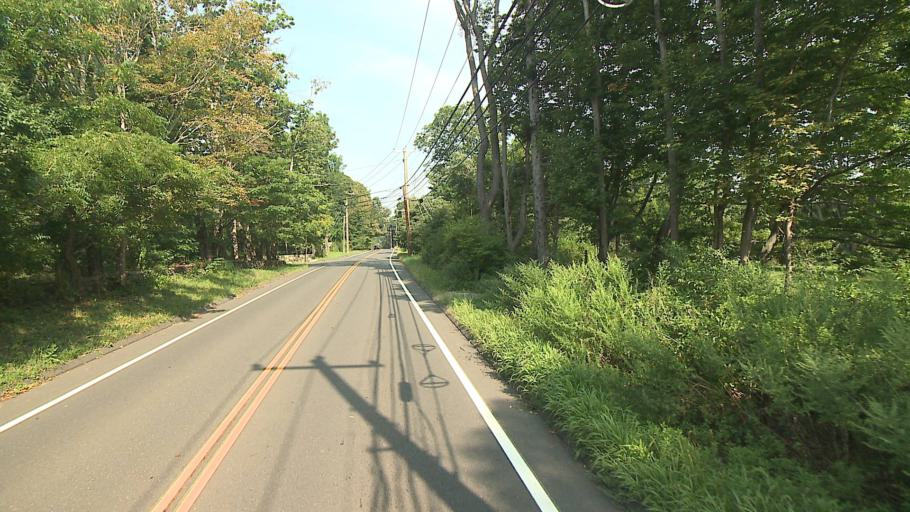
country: US
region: Connecticut
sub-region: Fairfield County
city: Wilton
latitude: 41.2228
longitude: -73.3967
